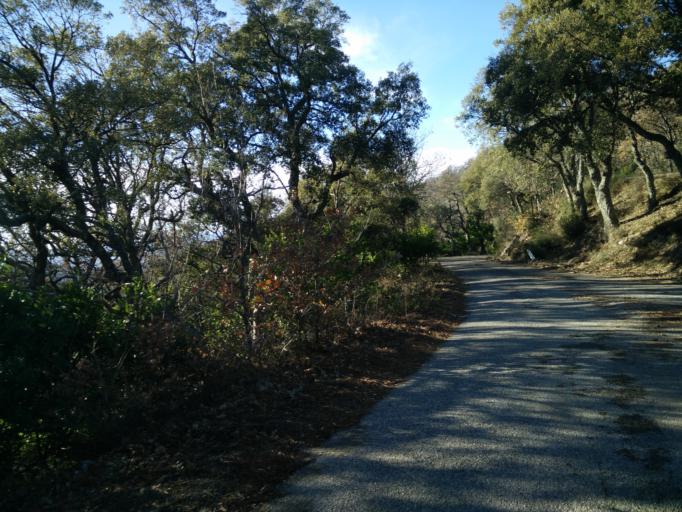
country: FR
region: Provence-Alpes-Cote d'Azur
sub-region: Departement du Var
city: Gonfaron
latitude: 43.2788
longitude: 6.2970
